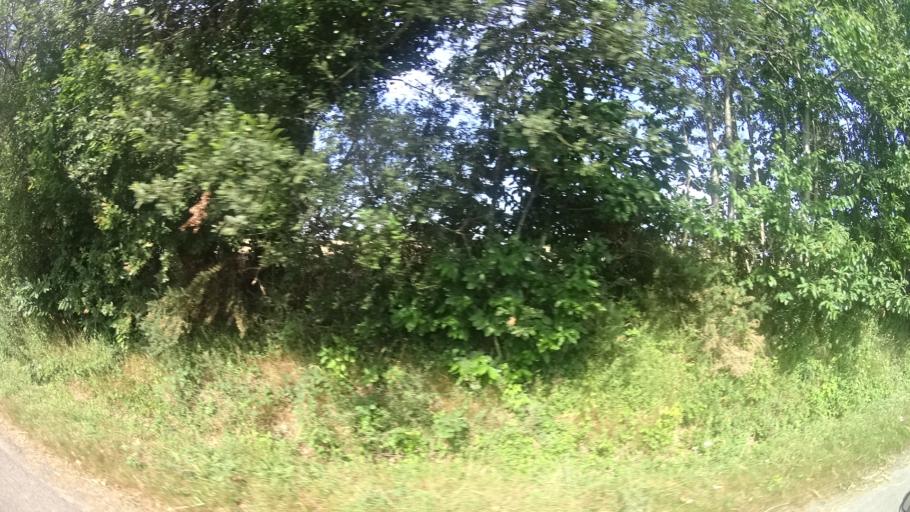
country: FR
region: Brittany
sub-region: Departement du Morbihan
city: Beganne
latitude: 47.6091
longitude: -2.2079
